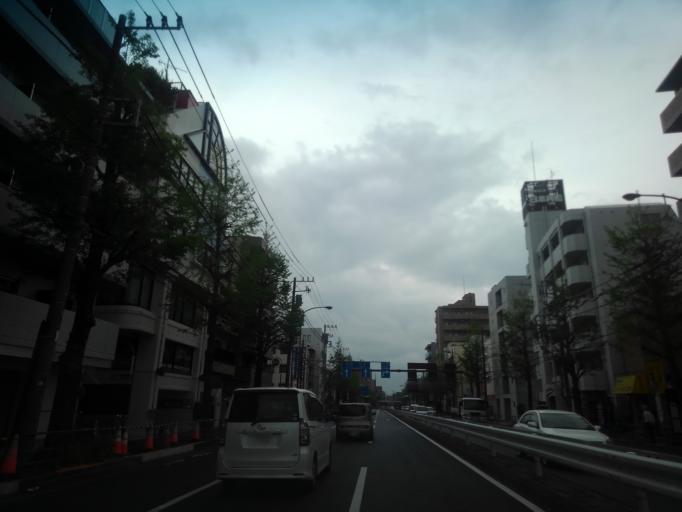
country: JP
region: Tokyo
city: Musashino
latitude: 35.7231
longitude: 139.5665
